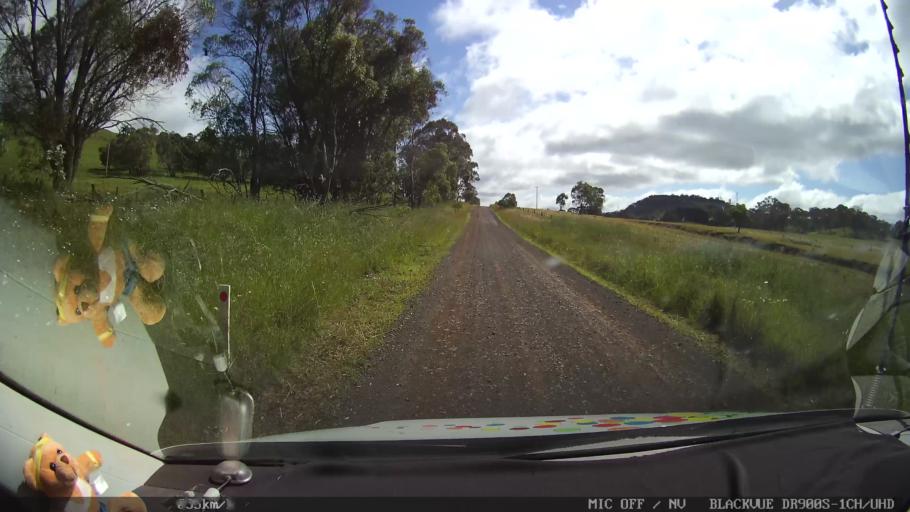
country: AU
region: New South Wales
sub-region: Guyra
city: Guyra
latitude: -30.0087
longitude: 151.6632
